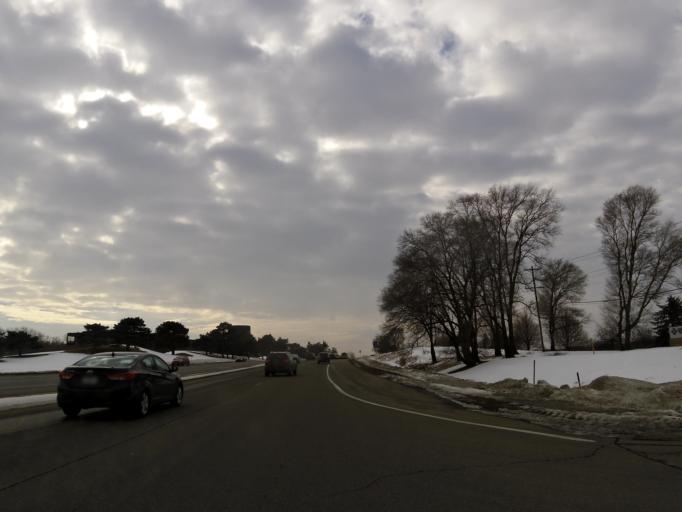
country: US
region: Minnesota
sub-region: Dakota County
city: Eagan
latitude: 44.8335
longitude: -93.1917
